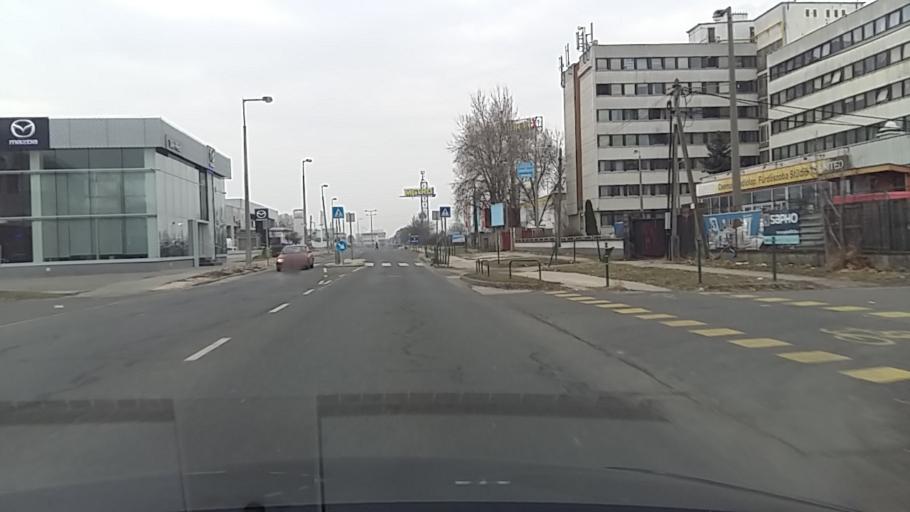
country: HU
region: Budapest
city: Budapest XX. keruelet
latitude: 47.4624
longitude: 19.1066
